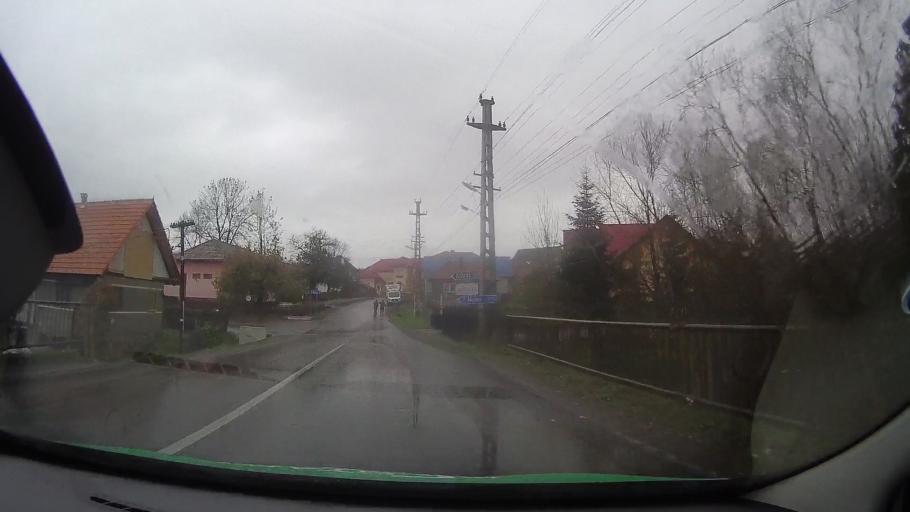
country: RO
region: Mures
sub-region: Comuna Vatava
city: Vatava
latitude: 46.9602
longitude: 24.7622
